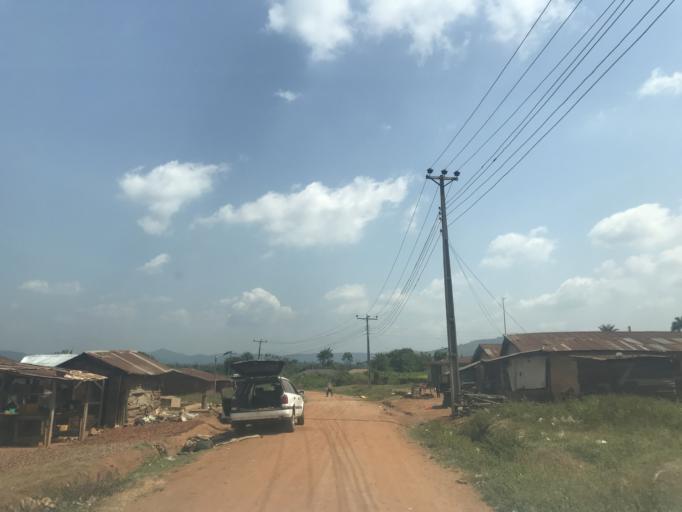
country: NG
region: Osun
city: Oke Mesi
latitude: 7.8864
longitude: 4.8873
